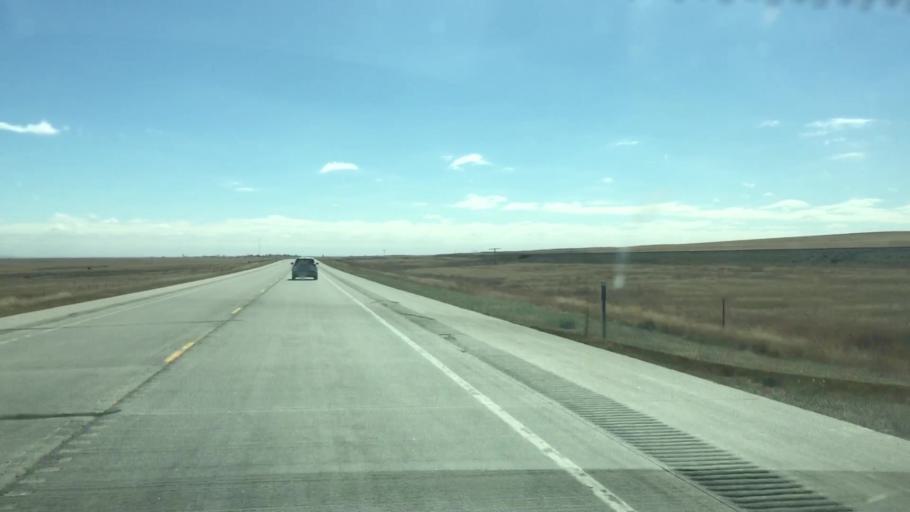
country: US
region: Colorado
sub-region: Lincoln County
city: Hugo
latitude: 39.1724
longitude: -103.5343
